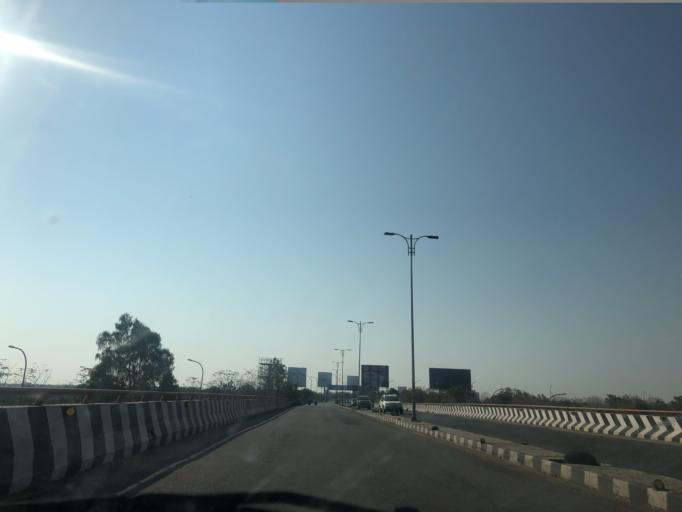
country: IN
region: Telangana
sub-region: Rangareddi
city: Sriramnagar
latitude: 17.2558
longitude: 78.3813
